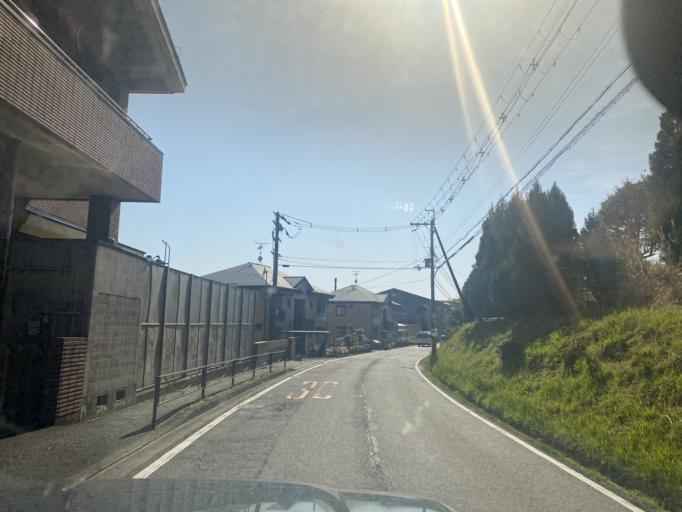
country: JP
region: Kyoto
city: Uji
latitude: 34.8559
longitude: 135.8630
